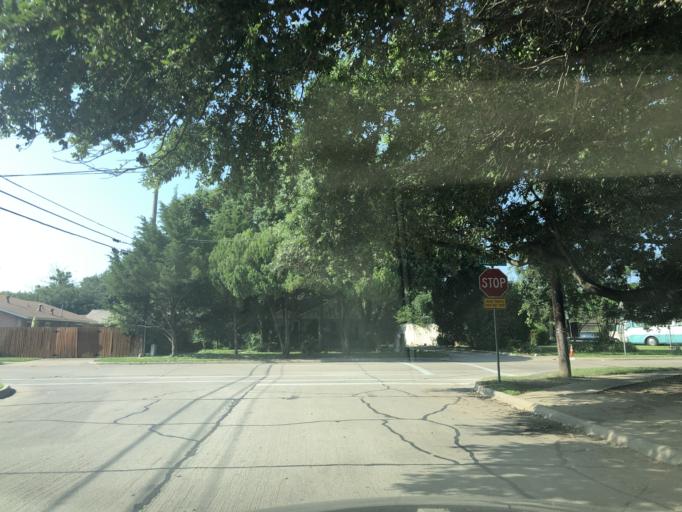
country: US
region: Texas
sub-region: Dallas County
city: Irving
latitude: 32.8108
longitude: -96.9817
